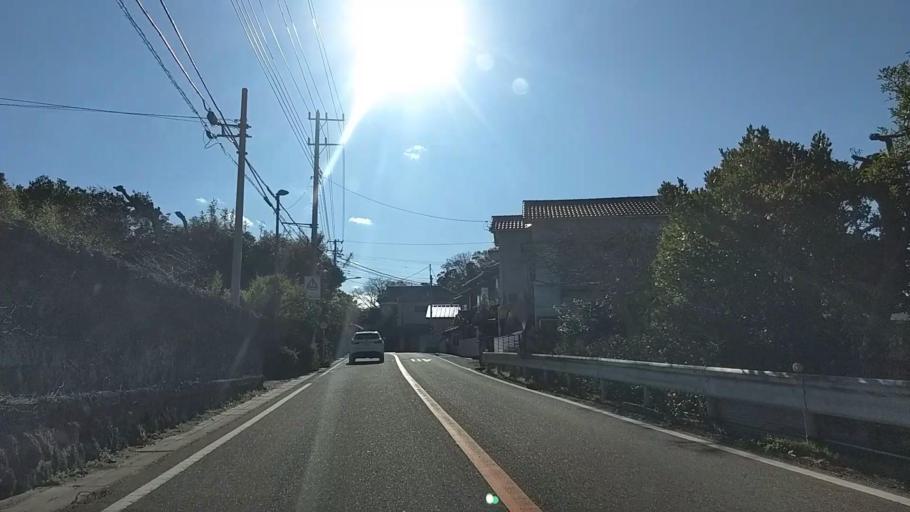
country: JP
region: Chiba
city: Futtsu
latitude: 35.1479
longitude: 139.8316
